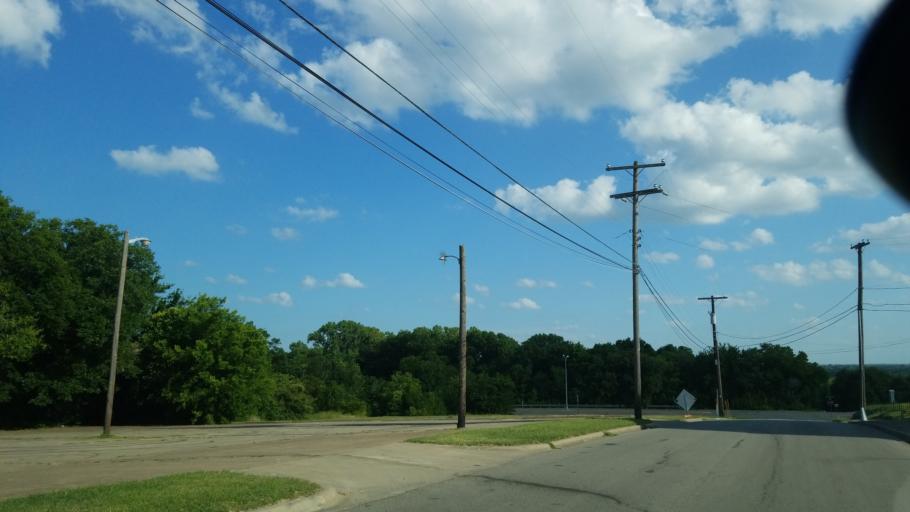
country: US
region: Texas
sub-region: Dallas County
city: Balch Springs
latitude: 32.7638
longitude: -96.7093
